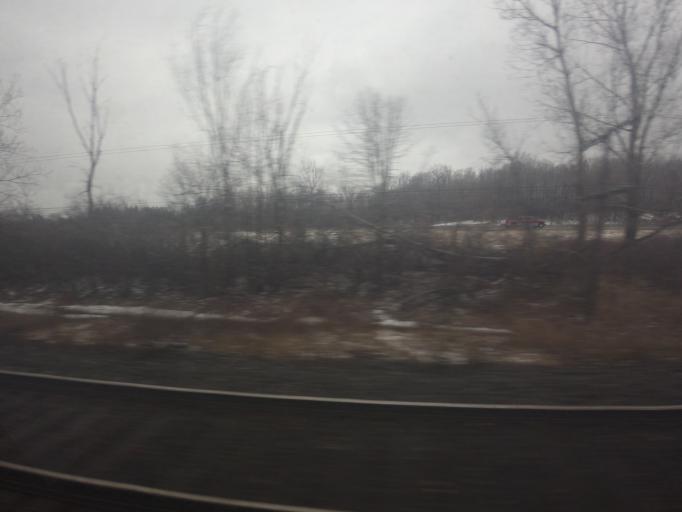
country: CA
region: Ontario
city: Kingston
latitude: 44.3174
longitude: -76.3761
